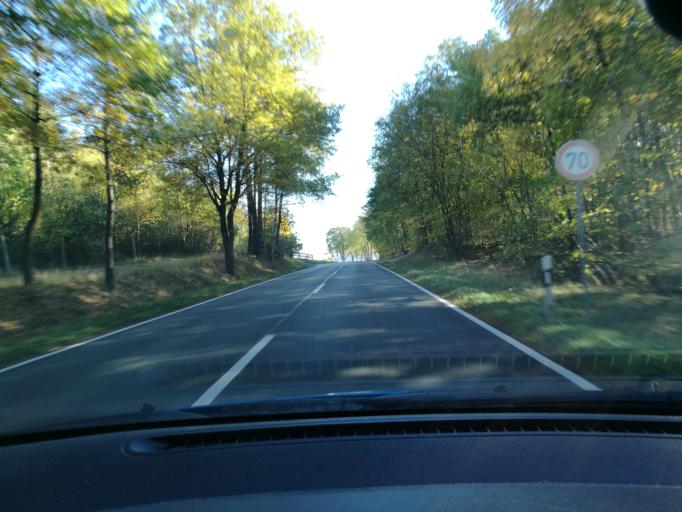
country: DE
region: Lower Saxony
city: Nahrendorf
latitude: 53.1715
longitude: 10.7788
